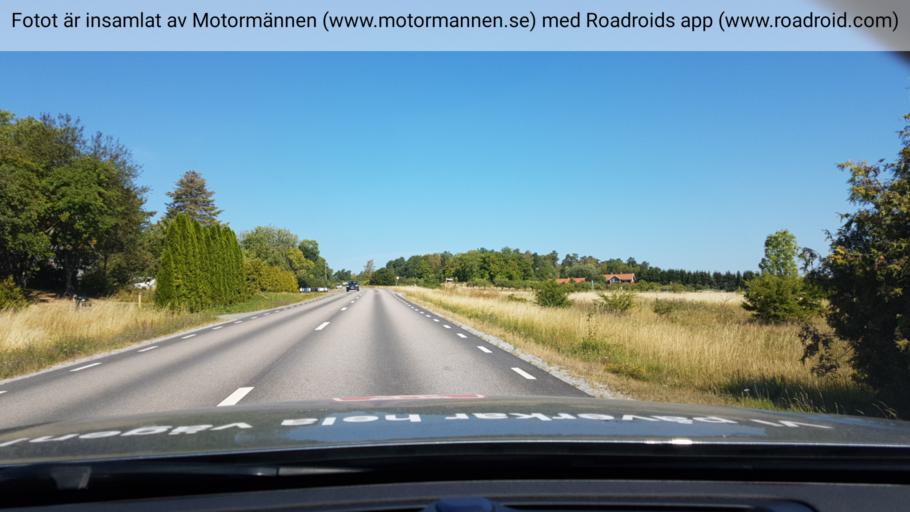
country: SE
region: Stockholm
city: Stenhamra
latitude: 59.3830
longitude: 17.5811
